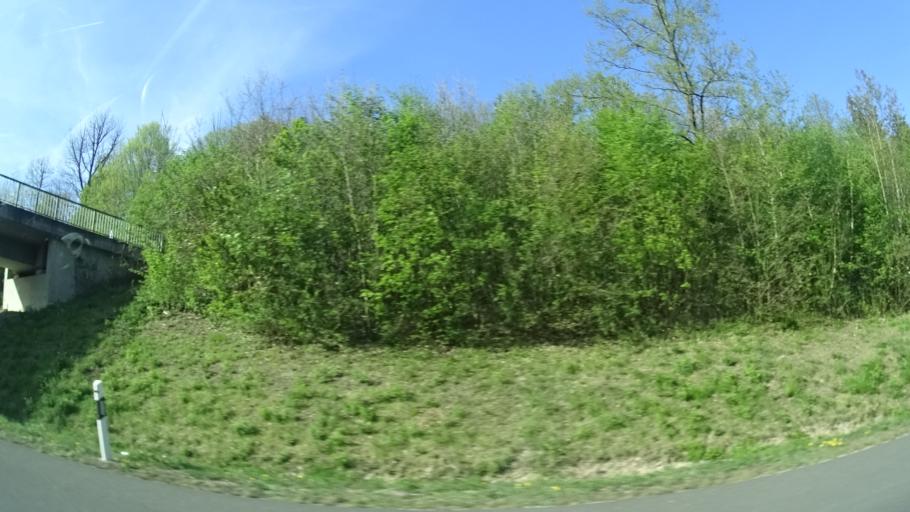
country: DE
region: Bavaria
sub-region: Regierungsbezirk Unterfranken
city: Donnersdorf
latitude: 50.0032
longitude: 10.4044
